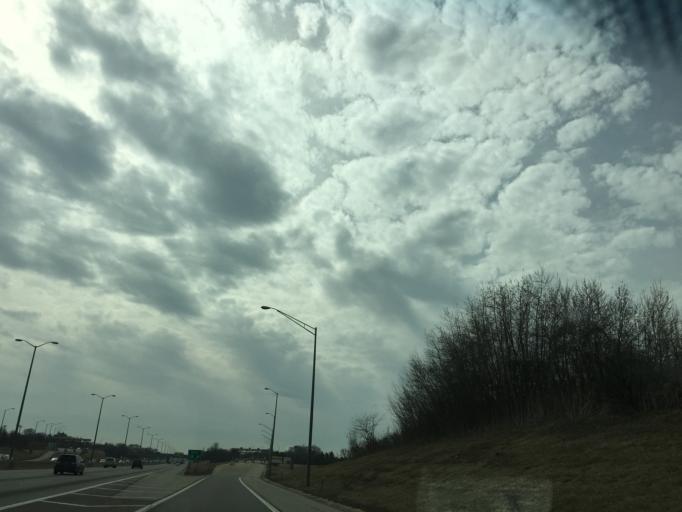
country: US
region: Illinois
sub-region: DuPage County
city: Woodridge
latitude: 41.7562
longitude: -88.0357
